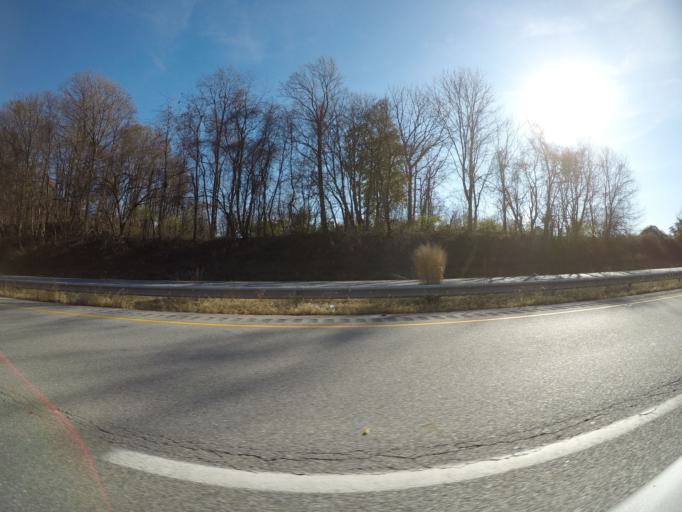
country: US
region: Pennsylvania
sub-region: Chester County
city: Coatesville
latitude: 39.9943
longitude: -75.8510
